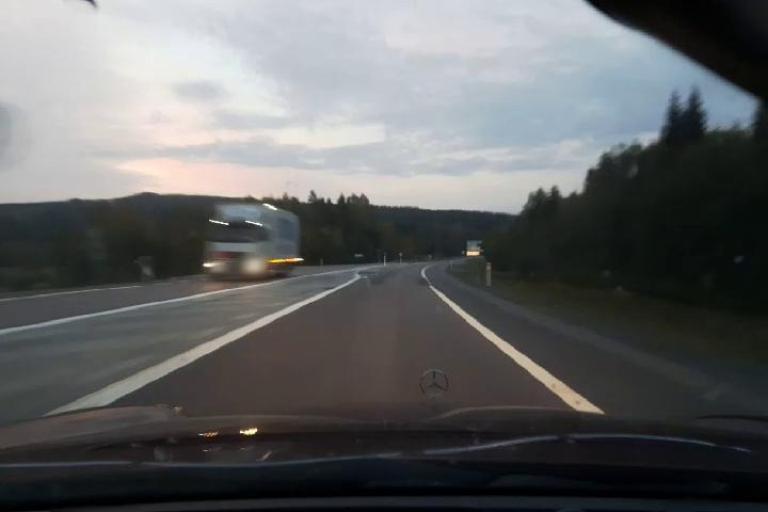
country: SE
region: Vaesternorrland
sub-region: Kramfors Kommun
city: Nordingra
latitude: 62.9517
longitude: 18.0962
